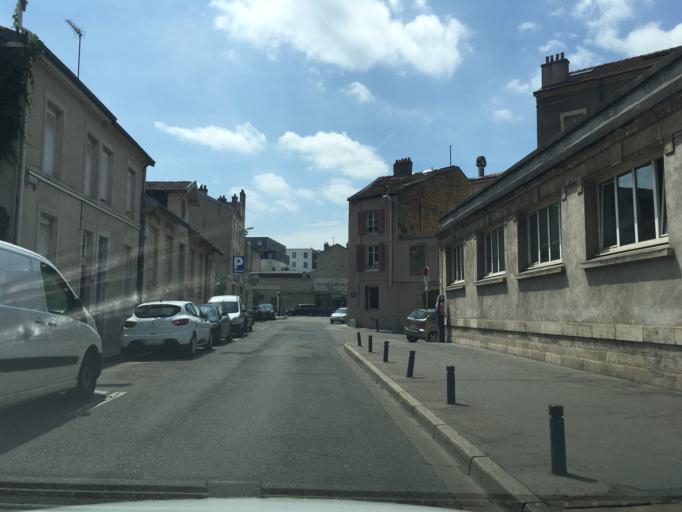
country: FR
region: Lorraine
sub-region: Departement de Meurthe-et-Moselle
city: Nancy
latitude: 48.6878
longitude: 6.1890
